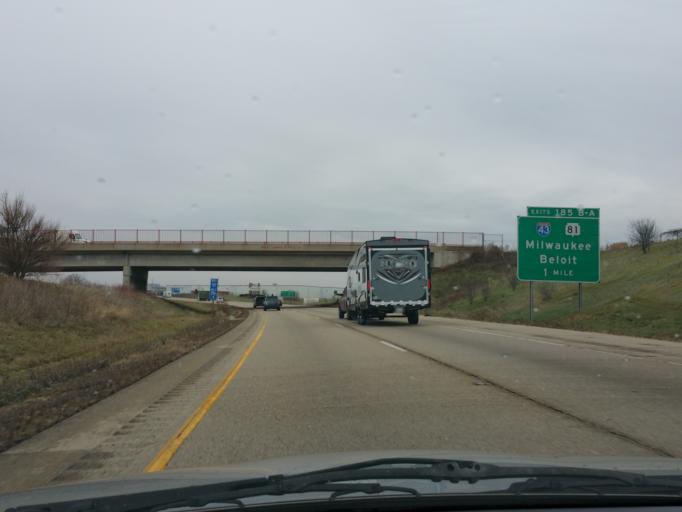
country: US
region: Wisconsin
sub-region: Rock County
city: Beloit
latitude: 42.5136
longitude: -88.9777
